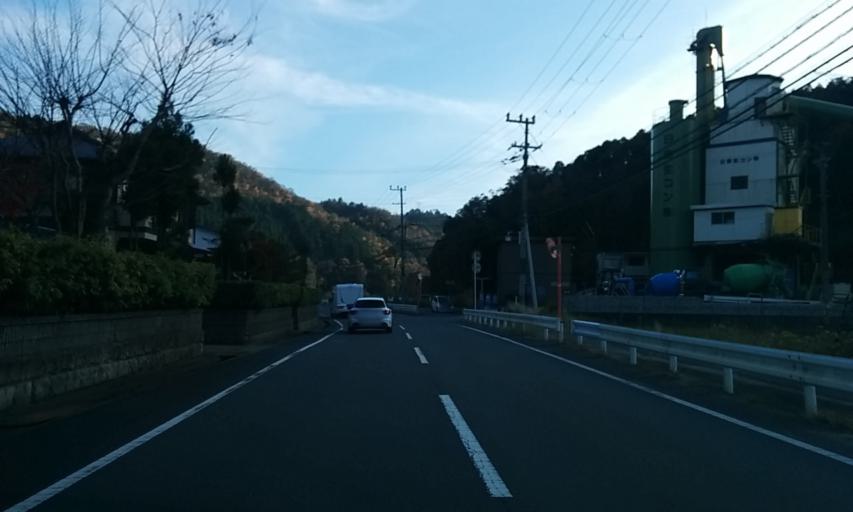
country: JP
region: Kyoto
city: Kameoka
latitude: 35.1760
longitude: 135.5135
